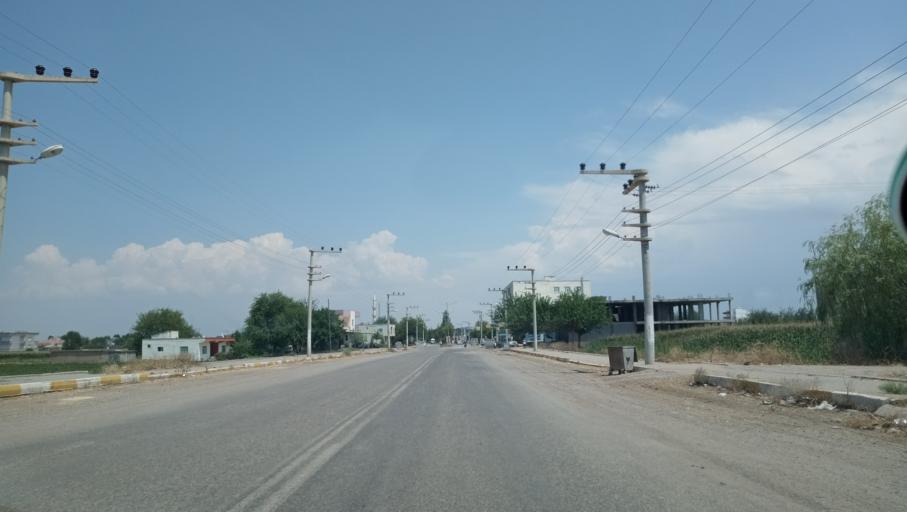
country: TR
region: Diyarbakir
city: Tepe
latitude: 37.7926
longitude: 40.7680
